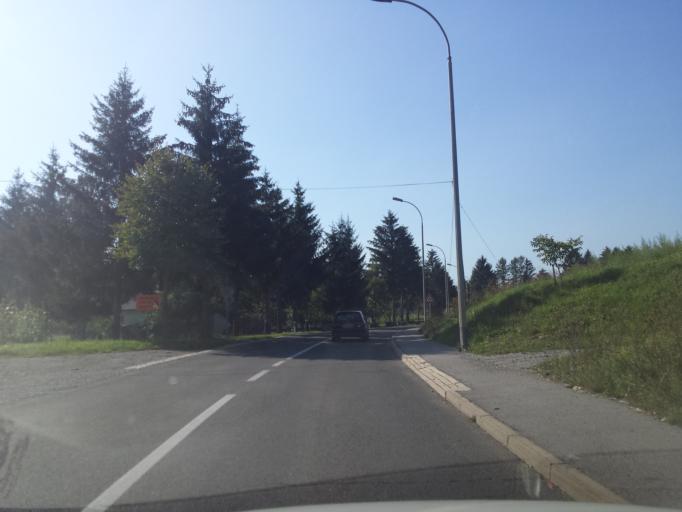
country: HR
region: Karlovacka
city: Ostarije
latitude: 45.2284
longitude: 15.2651
